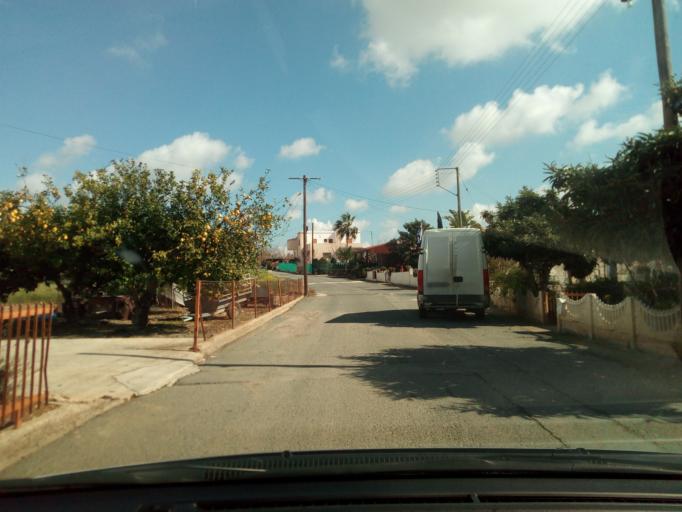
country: CY
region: Pafos
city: Empa
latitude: 34.8068
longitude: 32.4286
